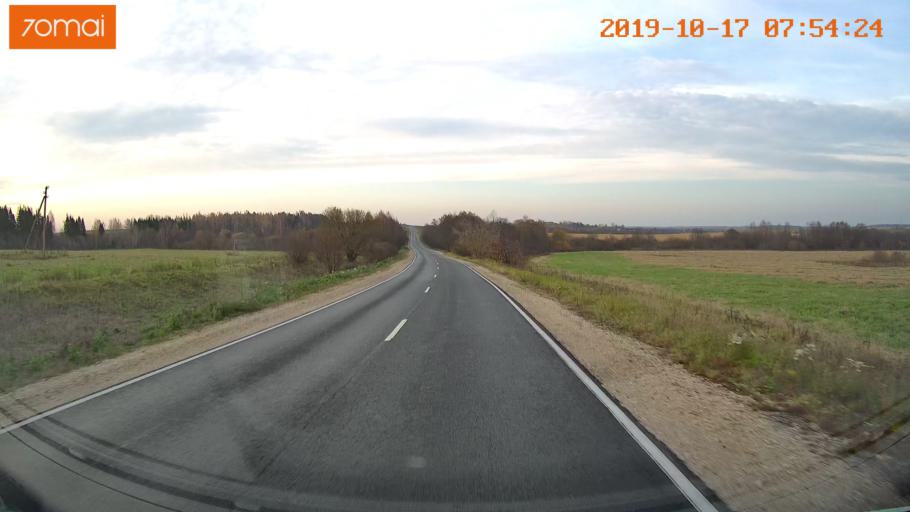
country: RU
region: Vladimir
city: Bavleny
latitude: 56.4503
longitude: 39.6067
